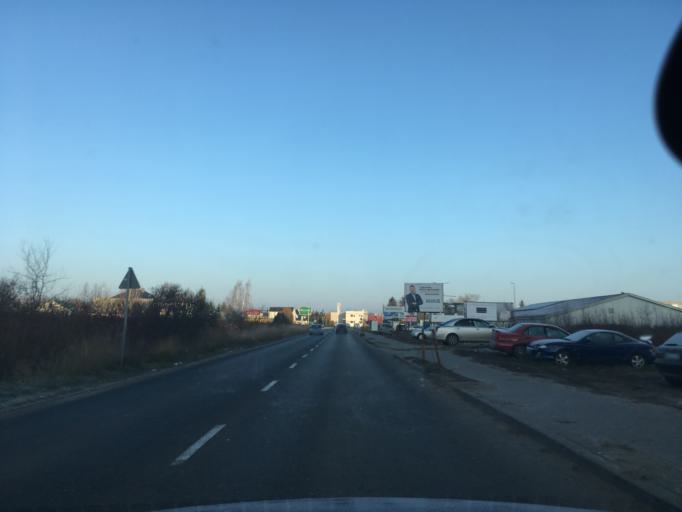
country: PL
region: Masovian Voivodeship
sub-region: Powiat piaseczynski
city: Piaseczno
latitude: 52.0805
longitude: 21.0084
